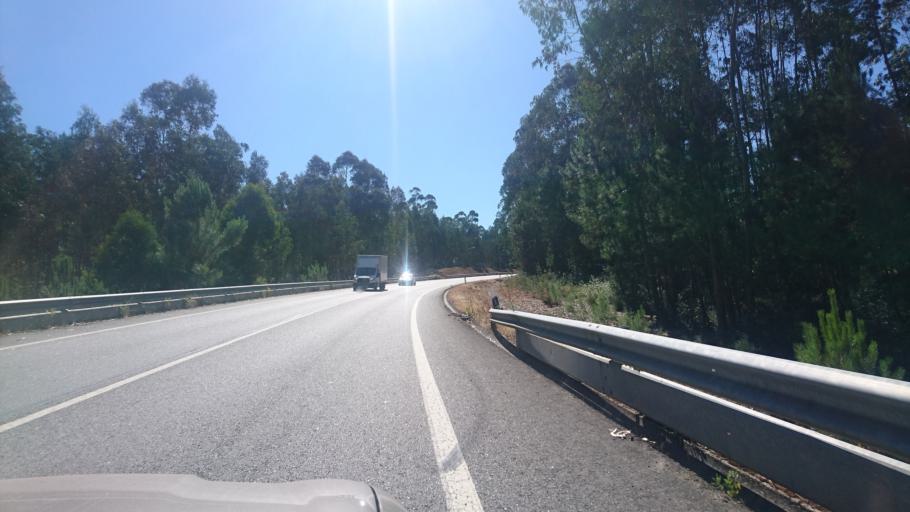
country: PT
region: Aveiro
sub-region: Santa Maria da Feira
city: Arrifana
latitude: 40.9258
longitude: -8.4914
